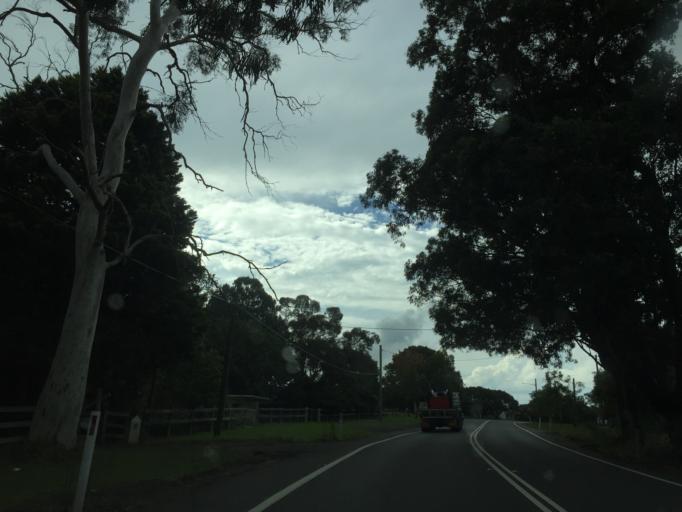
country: AU
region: New South Wales
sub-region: Hornsby Shire
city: Galston
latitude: -33.6556
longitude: 151.0397
